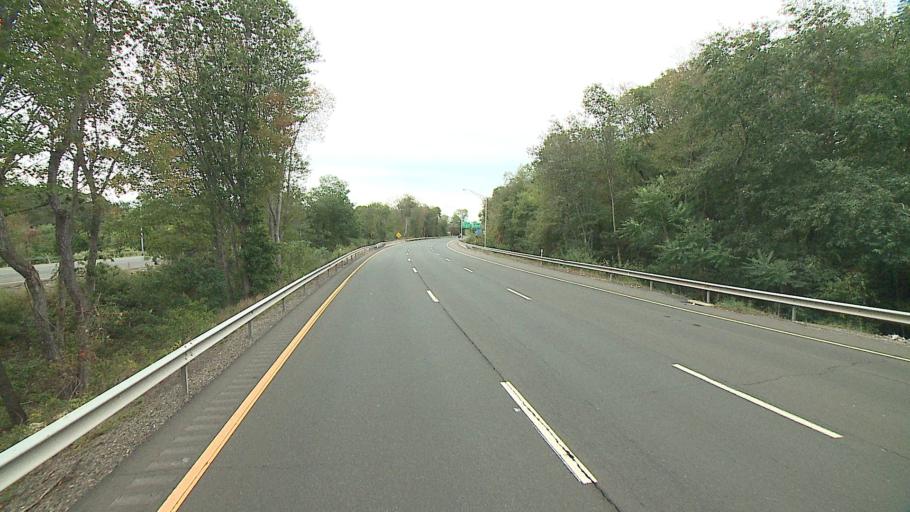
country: US
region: Connecticut
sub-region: Middlesex County
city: Old Saybrook Center
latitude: 41.3198
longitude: -72.3646
